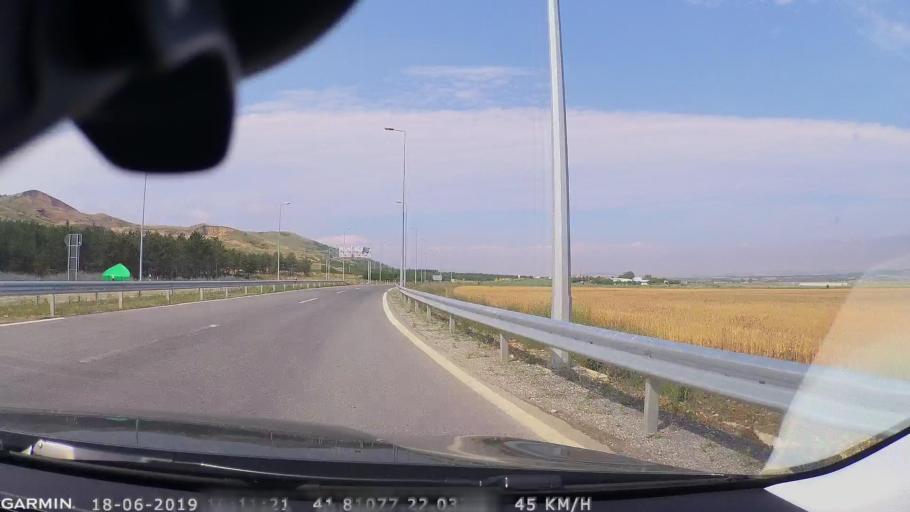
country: MK
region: Sveti Nikole
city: Sveti Nikole
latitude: 41.8292
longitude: 21.9995
